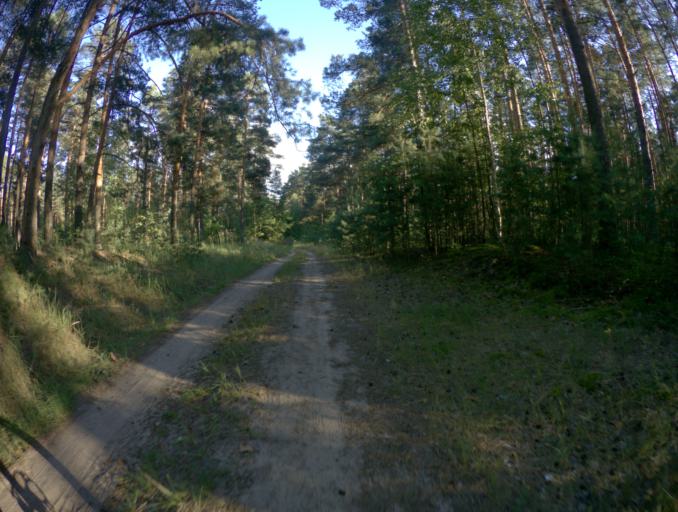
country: RU
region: Vladimir
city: Raduzhnyy
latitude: 56.0347
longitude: 40.3728
